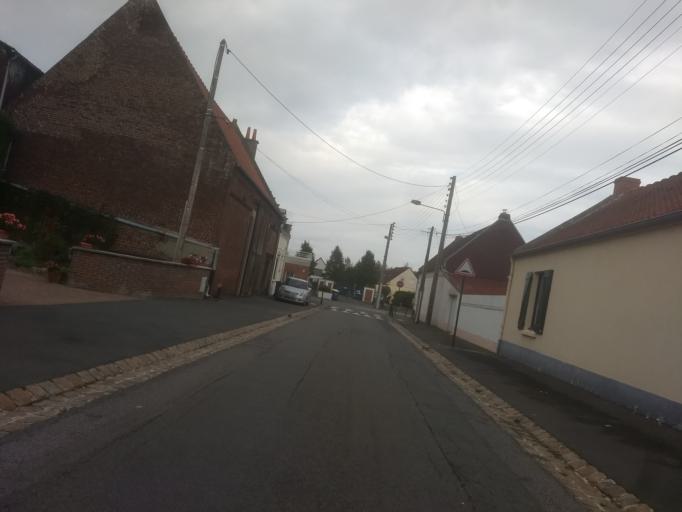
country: FR
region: Nord-Pas-de-Calais
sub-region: Departement du Pas-de-Calais
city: Achicourt
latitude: 50.2739
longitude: 2.7539
